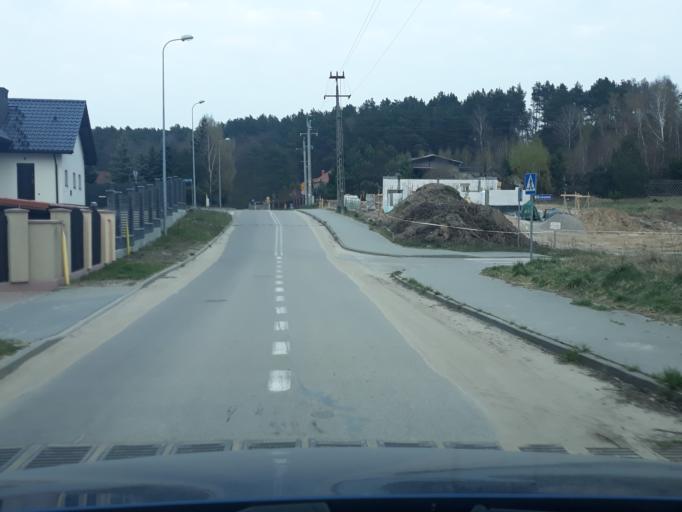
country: PL
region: Pomeranian Voivodeship
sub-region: Powiat chojnicki
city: Chojnice
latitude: 53.7282
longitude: 17.4970
